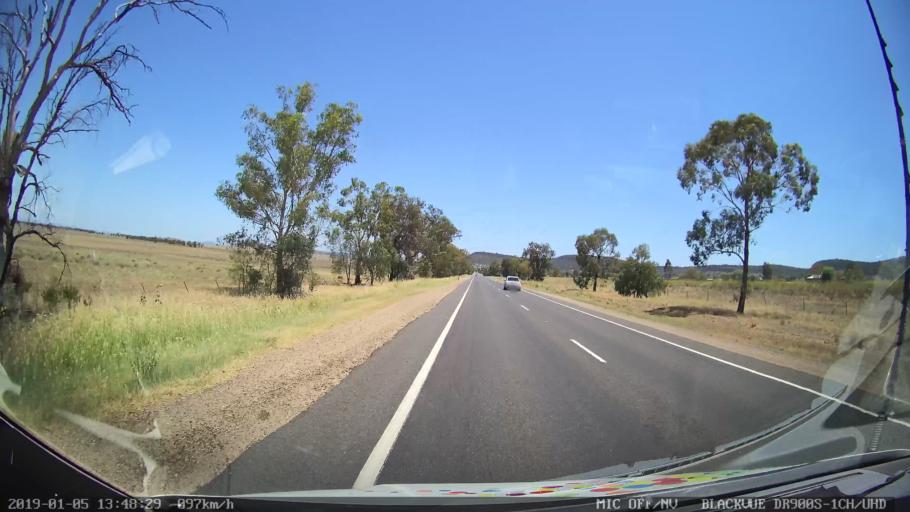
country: AU
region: New South Wales
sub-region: Gunnedah
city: Gunnedah
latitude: -31.0025
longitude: 150.2778
